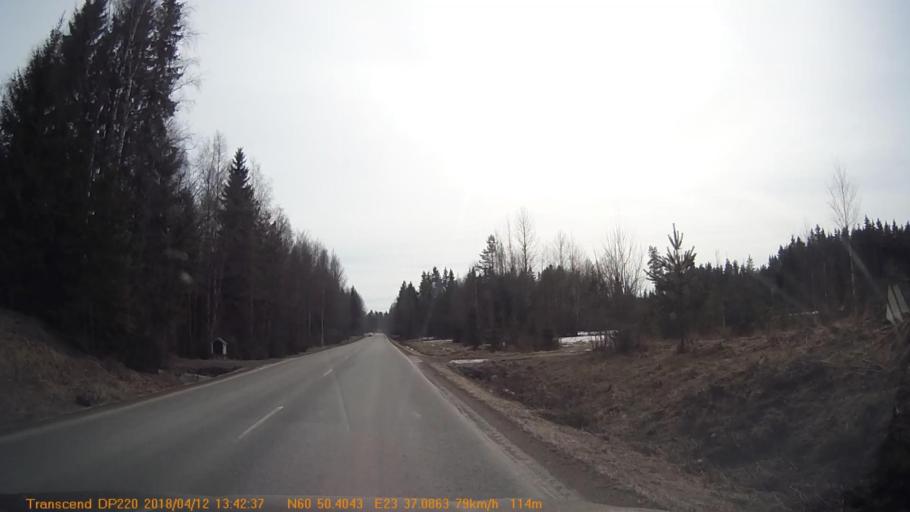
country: FI
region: Haeme
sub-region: Forssa
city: Forssa
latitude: 60.8394
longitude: 23.6181
